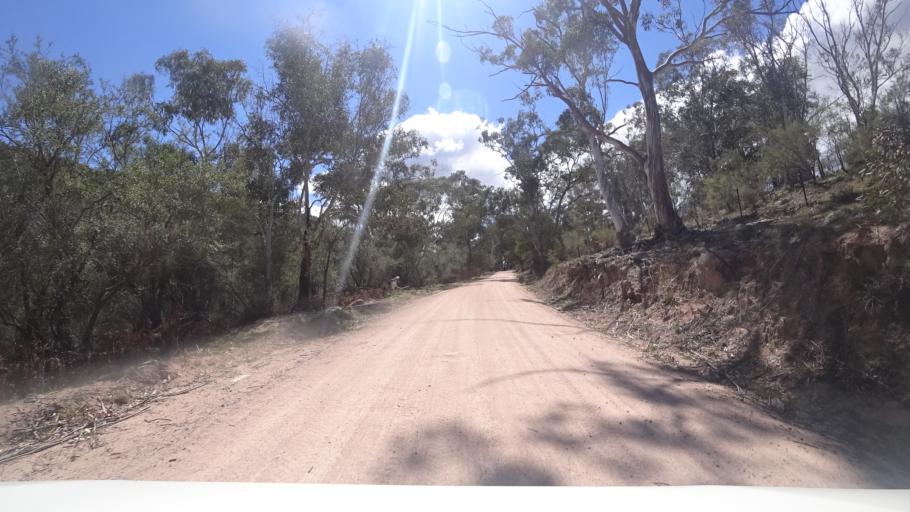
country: AU
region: New South Wales
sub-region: Oberon
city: Oberon
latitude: -33.5438
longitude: 149.9321
